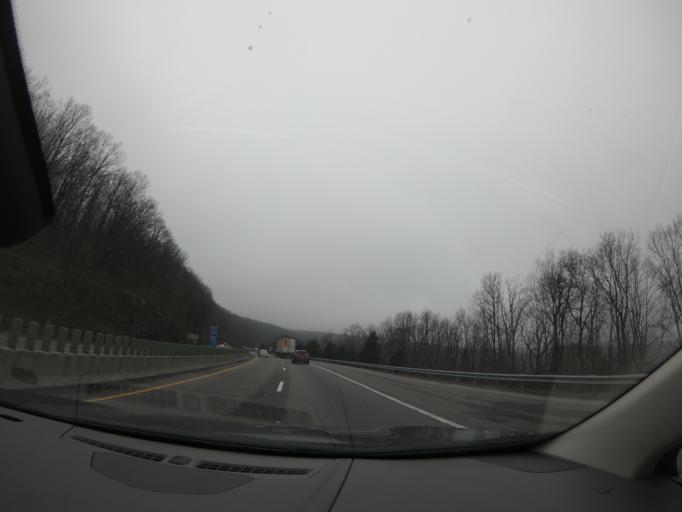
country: US
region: Tennessee
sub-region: Marion County
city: Monteagle
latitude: 35.2420
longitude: -85.8624
